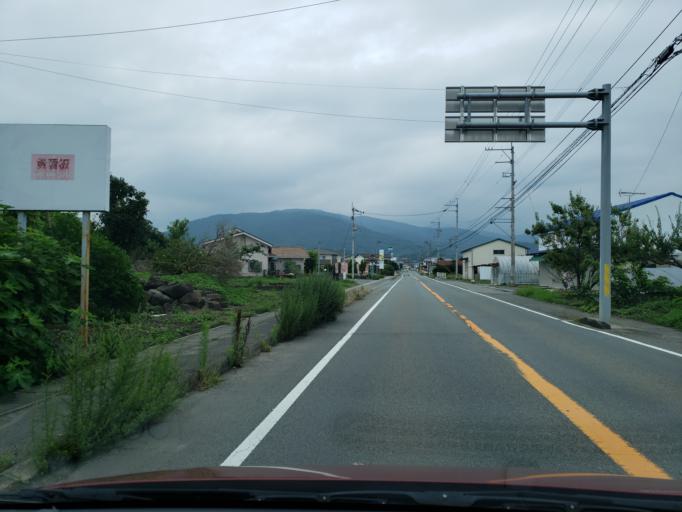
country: JP
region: Tokushima
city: Kamojimacho-jogejima
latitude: 34.1128
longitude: 134.3503
